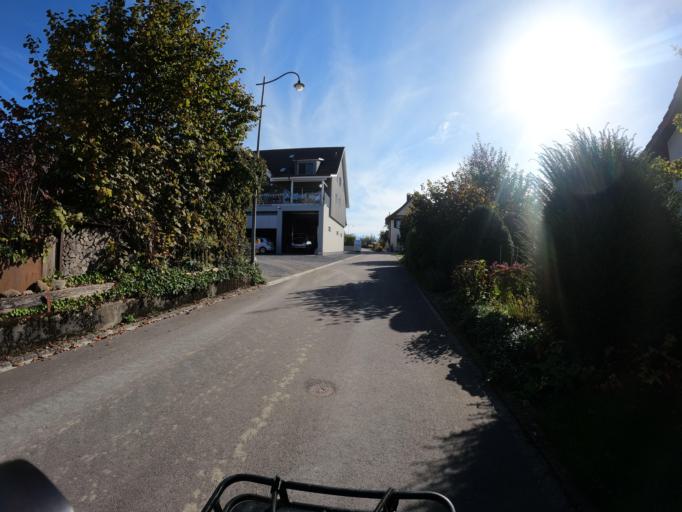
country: CH
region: Zug
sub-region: Zug
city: Steinhausen
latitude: 47.2200
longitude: 8.4971
